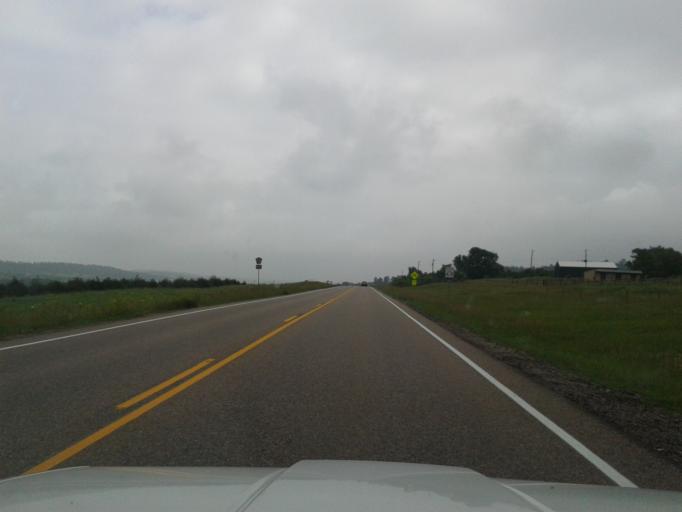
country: US
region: Colorado
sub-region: El Paso County
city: Woodmoor
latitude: 39.1741
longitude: -104.7388
